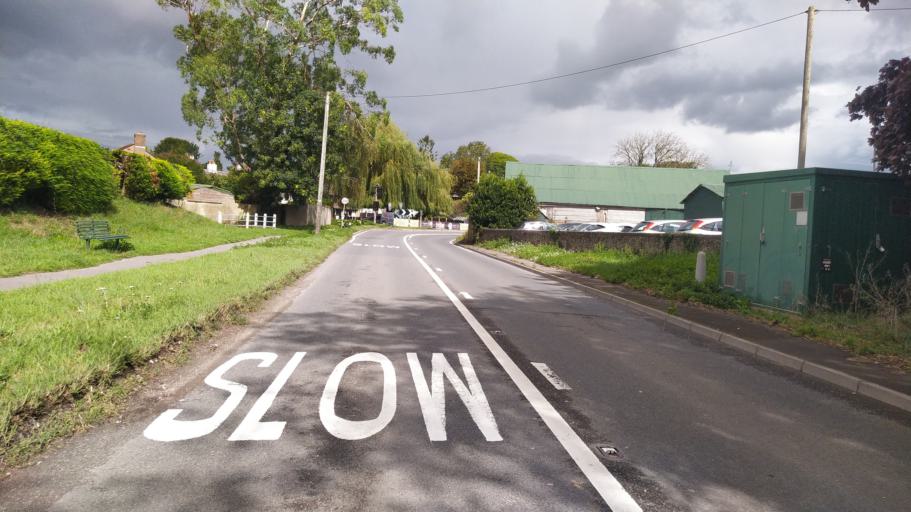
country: GB
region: England
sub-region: Dorset
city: Blandford Forum
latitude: 50.8819
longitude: -2.1345
